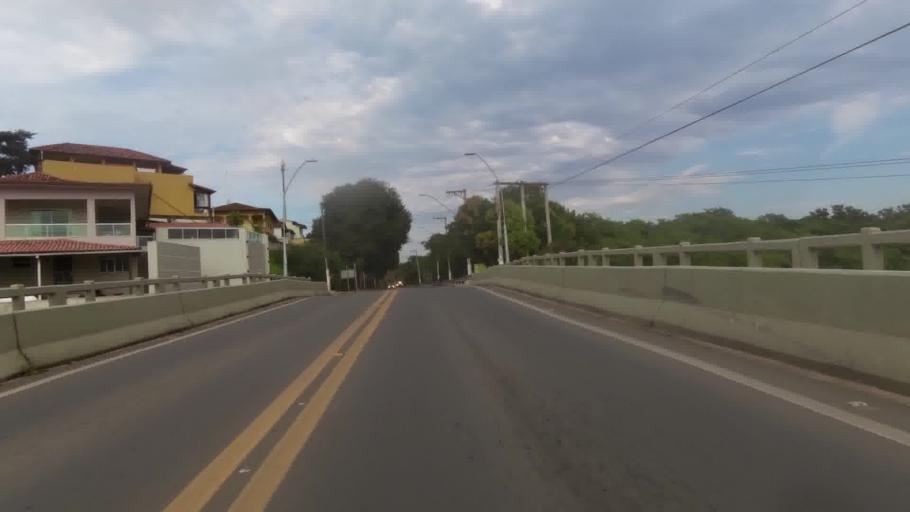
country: BR
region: Espirito Santo
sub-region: Piuma
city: Piuma
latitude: -20.8061
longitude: -40.6560
